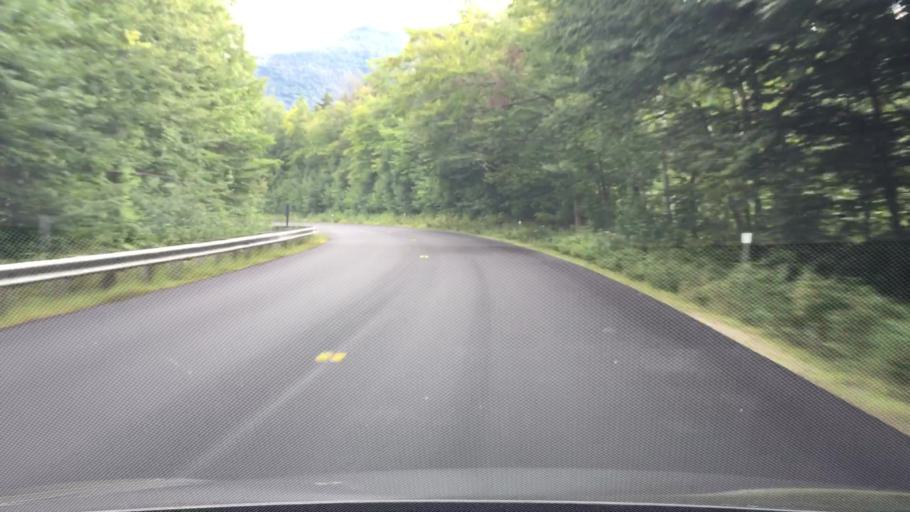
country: US
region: New Hampshire
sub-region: Carroll County
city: Sandwich
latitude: 44.0109
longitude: -71.4281
